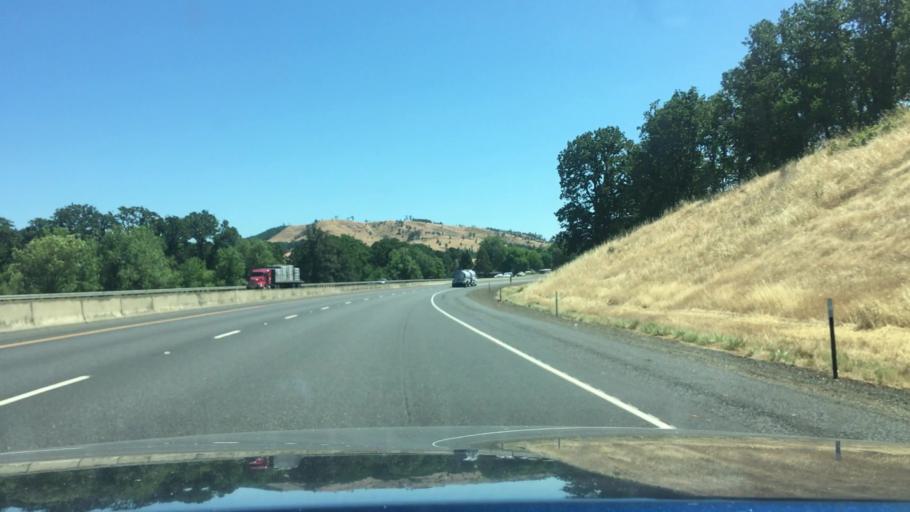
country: US
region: Oregon
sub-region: Douglas County
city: Sutherlin
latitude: 43.4734
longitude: -123.3170
